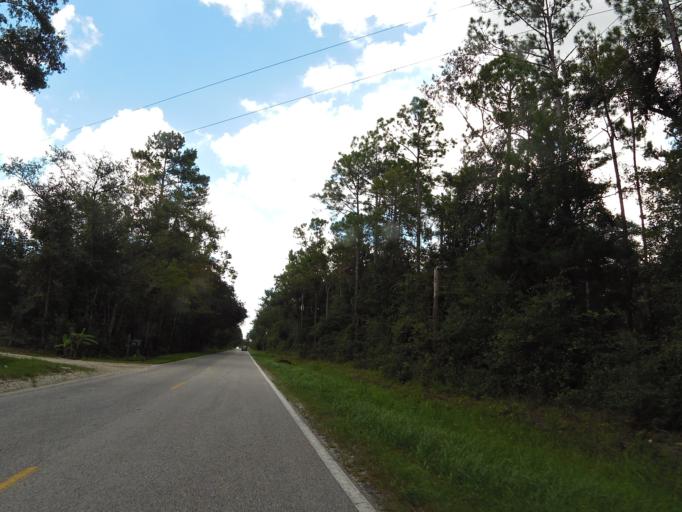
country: US
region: Florida
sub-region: Putnam County
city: East Palatka
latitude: 29.7748
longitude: -81.4837
